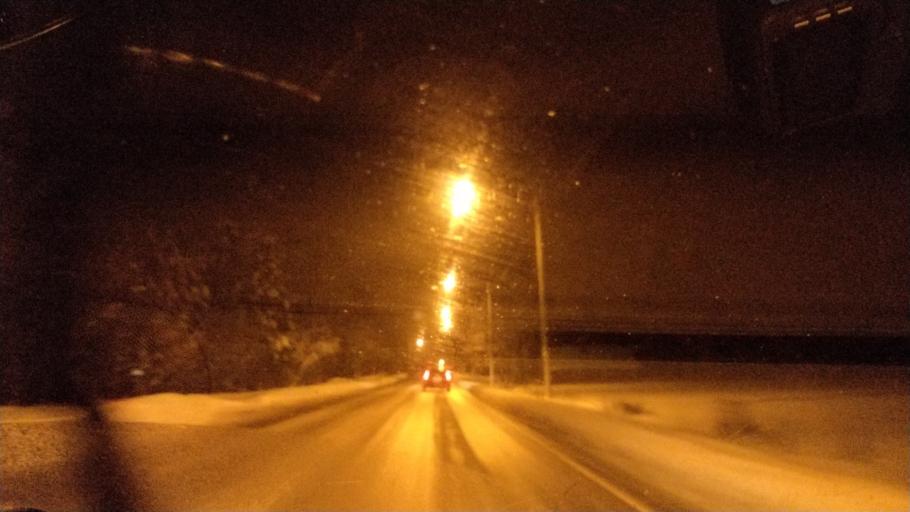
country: FI
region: Lapland
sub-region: Rovaniemi
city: Rovaniemi
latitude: 66.2644
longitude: 25.3372
